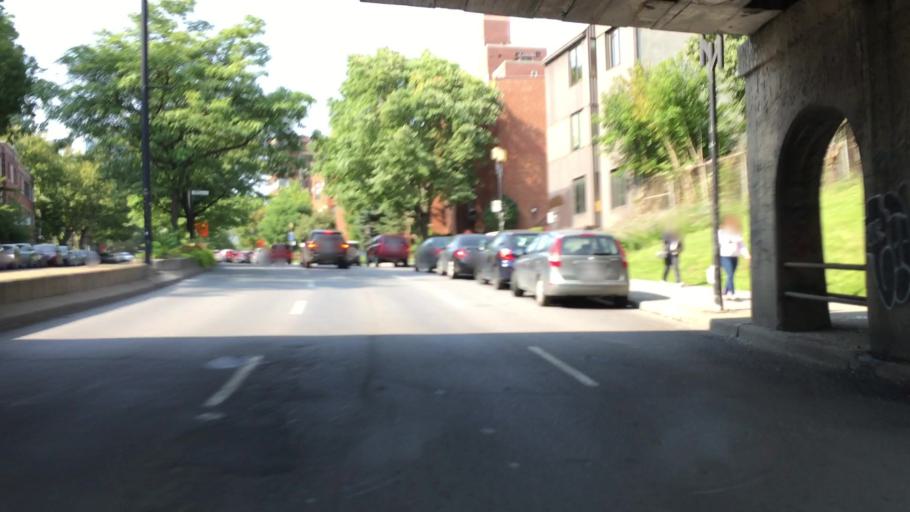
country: CA
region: Quebec
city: Westmount
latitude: 45.4868
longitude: -73.5814
